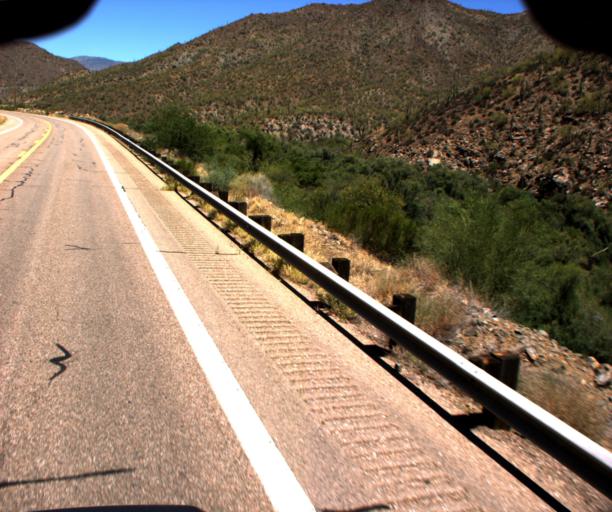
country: US
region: Arizona
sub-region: Pinal County
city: Kearny
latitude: 33.0558
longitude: -110.7192
